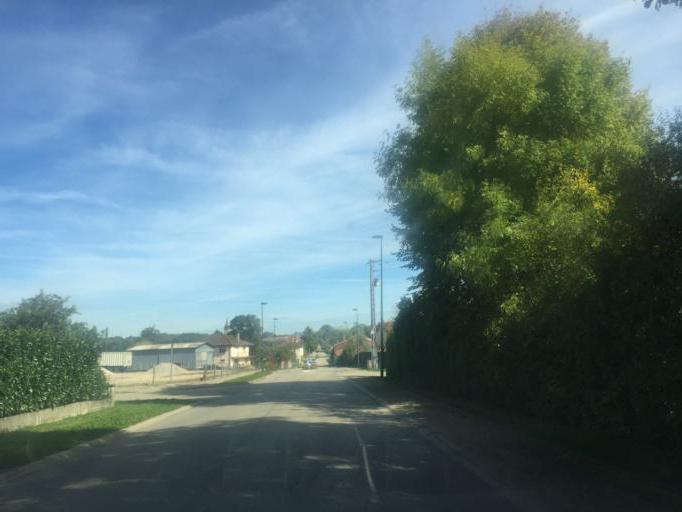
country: FR
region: Rhone-Alpes
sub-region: Departement de l'Ain
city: Marboz
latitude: 46.4087
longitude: 5.2581
